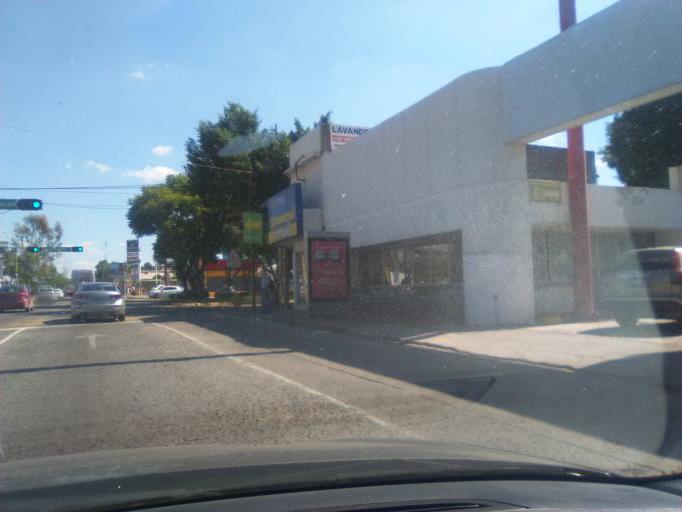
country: MX
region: Guanajuato
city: Leon
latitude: 21.1109
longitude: -101.6471
